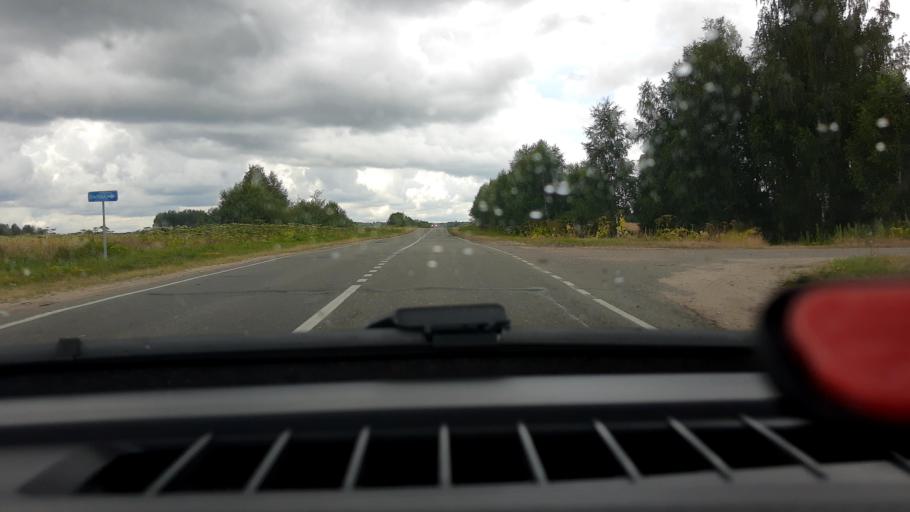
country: RU
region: Nizjnij Novgorod
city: Sitniki
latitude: 56.4977
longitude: 43.9999
